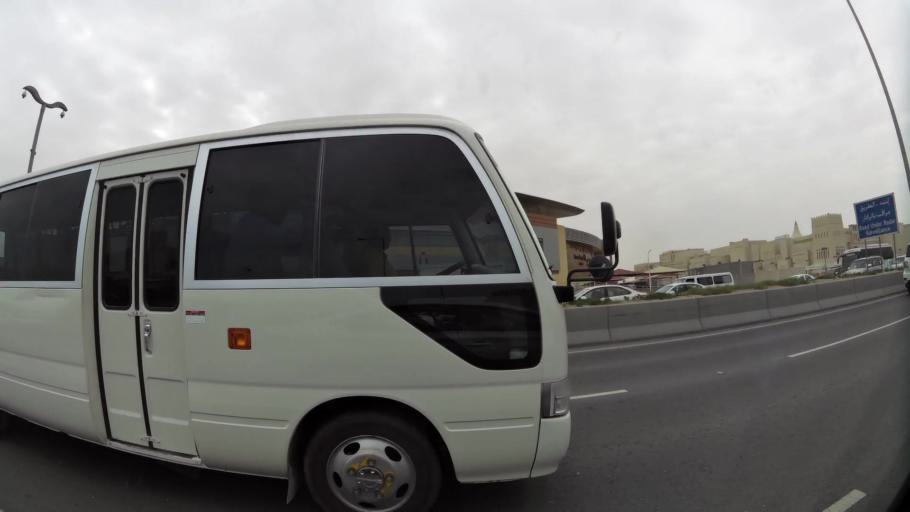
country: QA
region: Baladiyat ar Rayyan
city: Ar Rayyan
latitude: 25.3343
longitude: 51.4631
